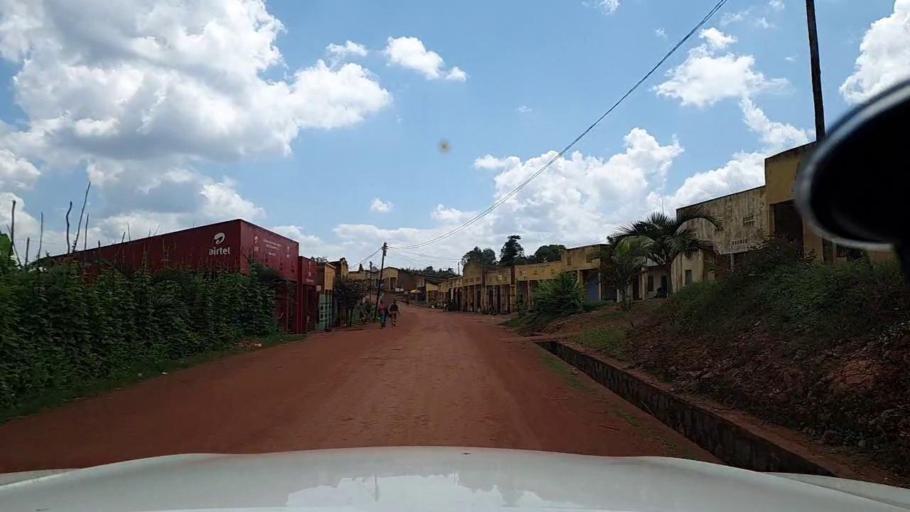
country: RW
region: Kigali
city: Kigali
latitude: -1.8036
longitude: 29.8418
